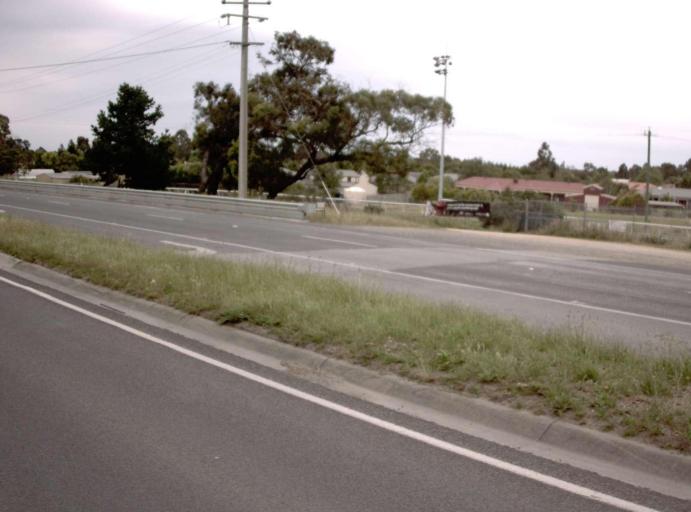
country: AU
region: Victoria
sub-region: Casey
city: Cranbourne
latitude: -38.1212
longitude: 145.2883
